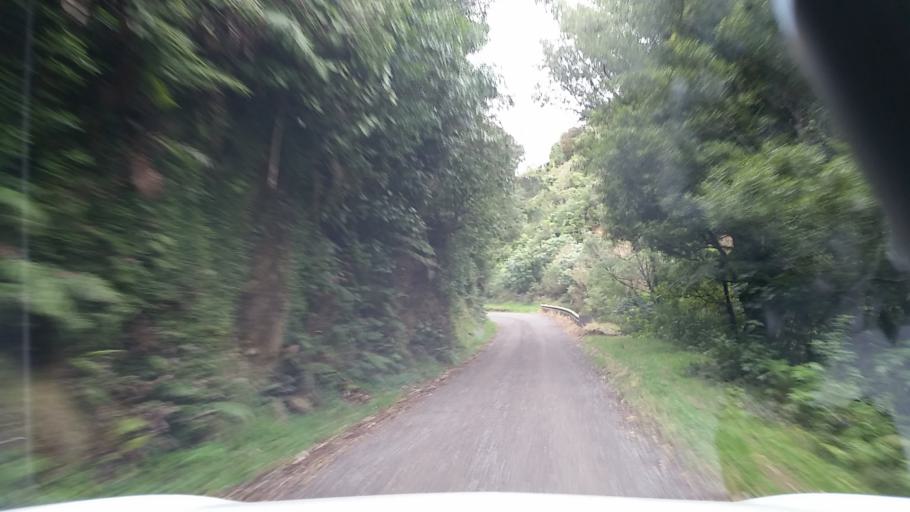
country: NZ
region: Bay of Plenty
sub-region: Rotorua District
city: Rotorua
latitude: -38.1591
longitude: 176.3669
